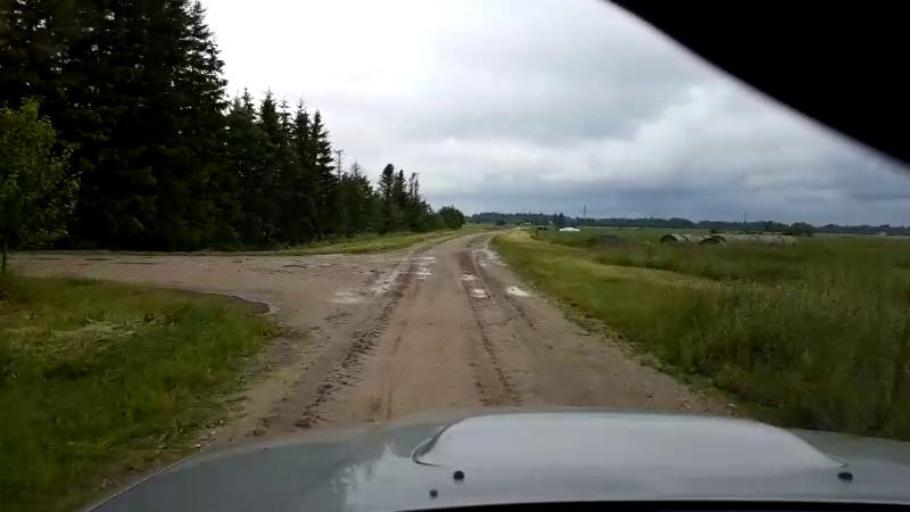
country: EE
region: Paernumaa
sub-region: Halinga vald
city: Parnu-Jaagupi
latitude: 58.5337
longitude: 24.5763
